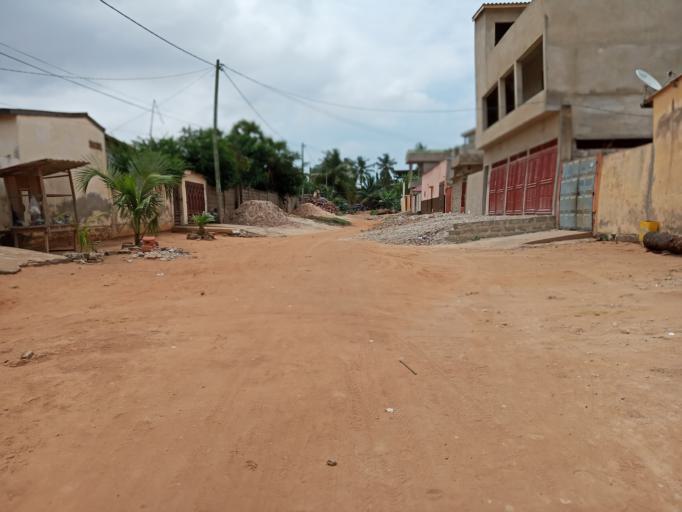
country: TG
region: Maritime
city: Lome
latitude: 6.1827
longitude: 1.1733
